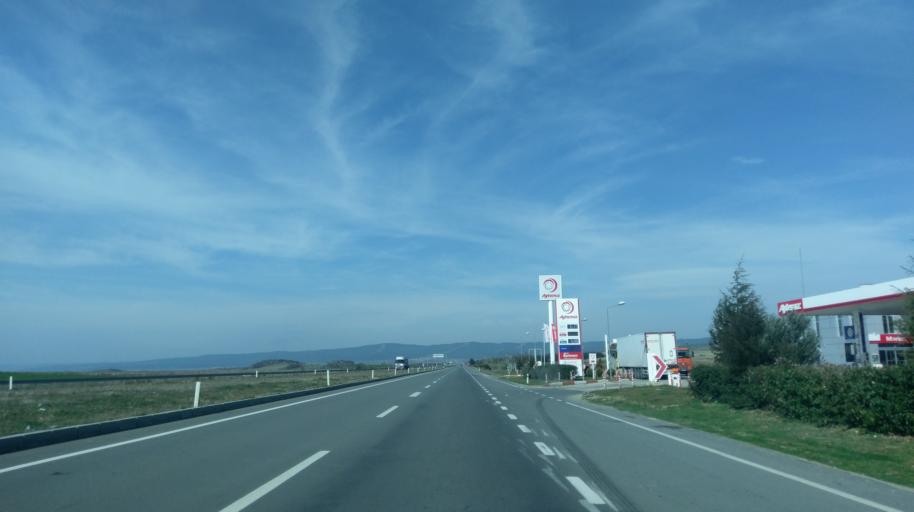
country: TR
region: Canakkale
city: Evrese
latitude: 40.6396
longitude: 26.8590
